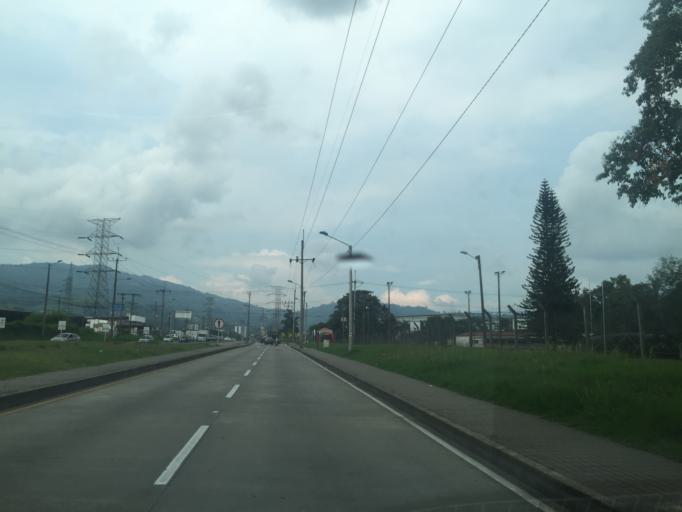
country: CO
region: Risaralda
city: Dos Quebradas
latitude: 4.8328
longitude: -75.6795
